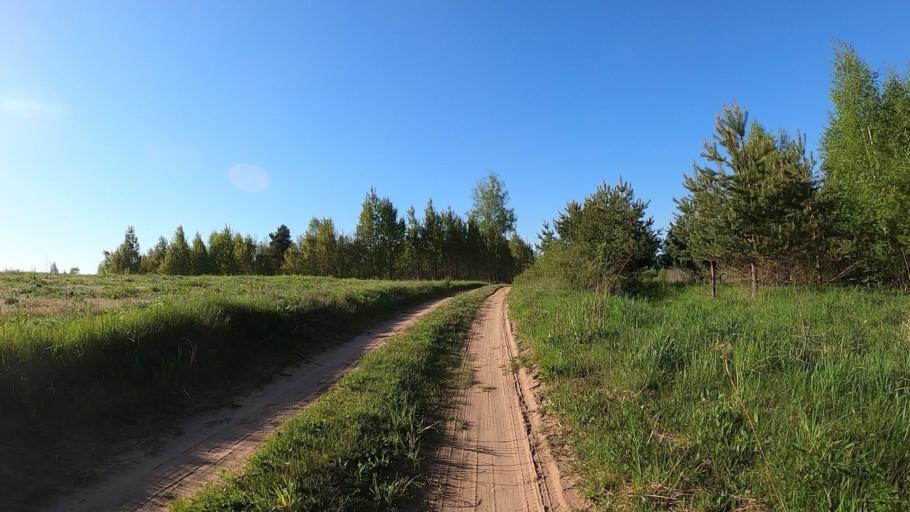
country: LV
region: Baldone
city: Baldone
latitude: 56.7704
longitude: 24.3286
